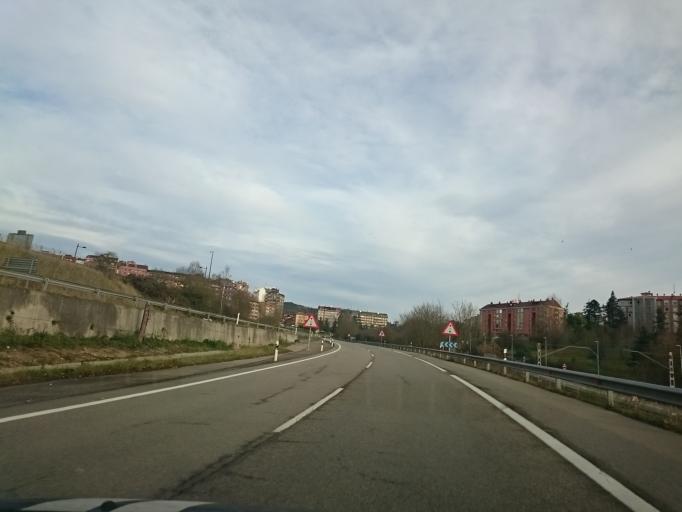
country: ES
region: Asturias
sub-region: Province of Asturias
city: Oviedo
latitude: 43.3503
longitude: -5.8568
